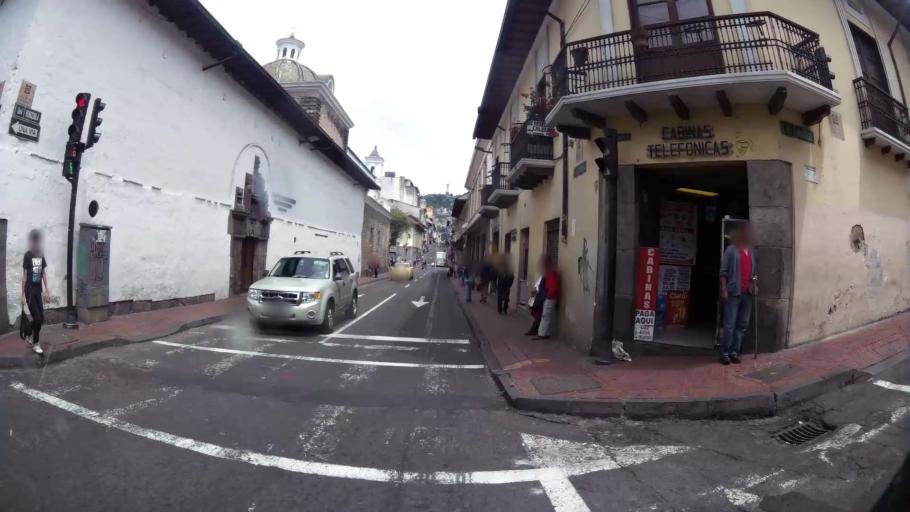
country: EC
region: Pichincha
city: Quito
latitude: -0.2181
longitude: -78.5100
